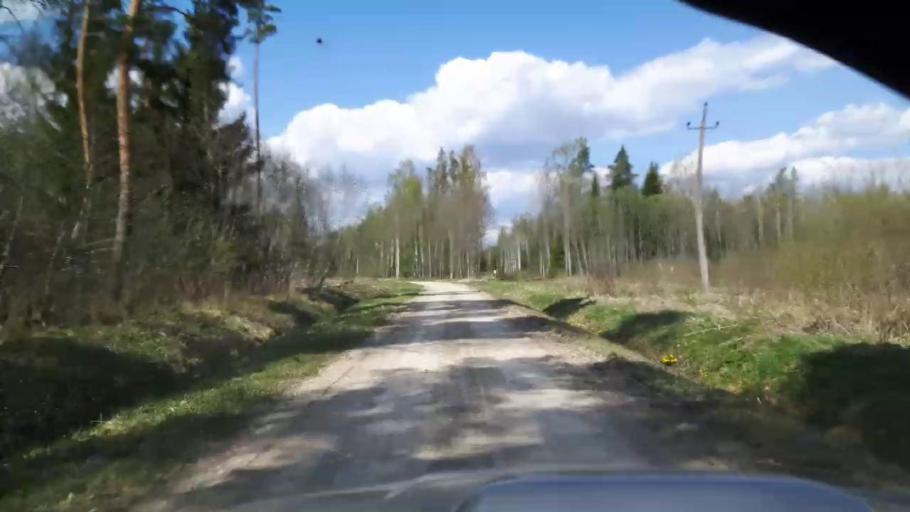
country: EE
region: Paernumaa
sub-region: Tootsi vald
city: Tootsi
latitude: 58.4527
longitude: 24.8935
